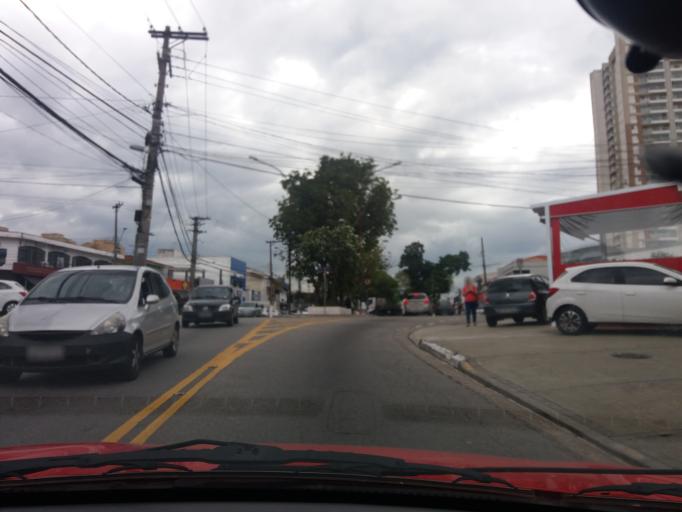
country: BR
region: Sao Paulo
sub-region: Osasco
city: Osasco
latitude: -23.5780
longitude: -46.7409
